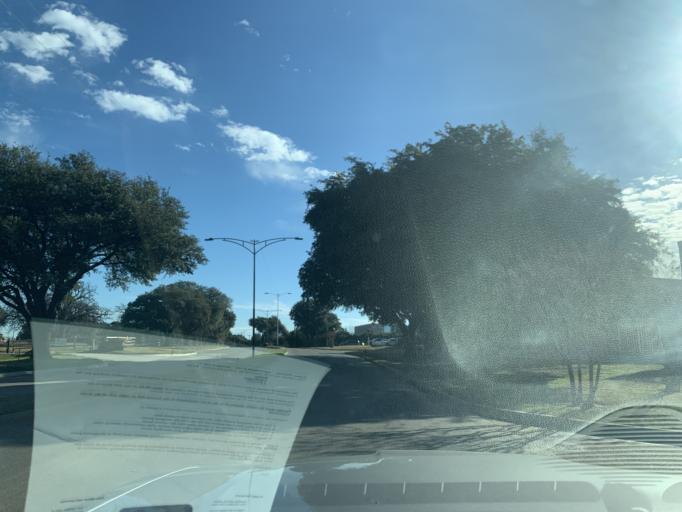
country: US
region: Texas
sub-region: Tarrant County
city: Arlington
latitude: 32.7619
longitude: -97.0608
